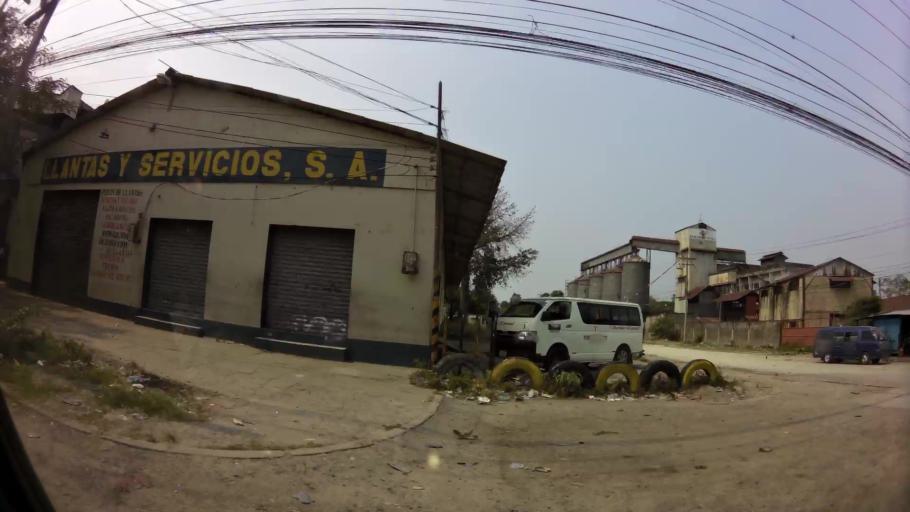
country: HN
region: Cortes
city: San Pedro Sula
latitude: 15.4881
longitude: -88.0262
